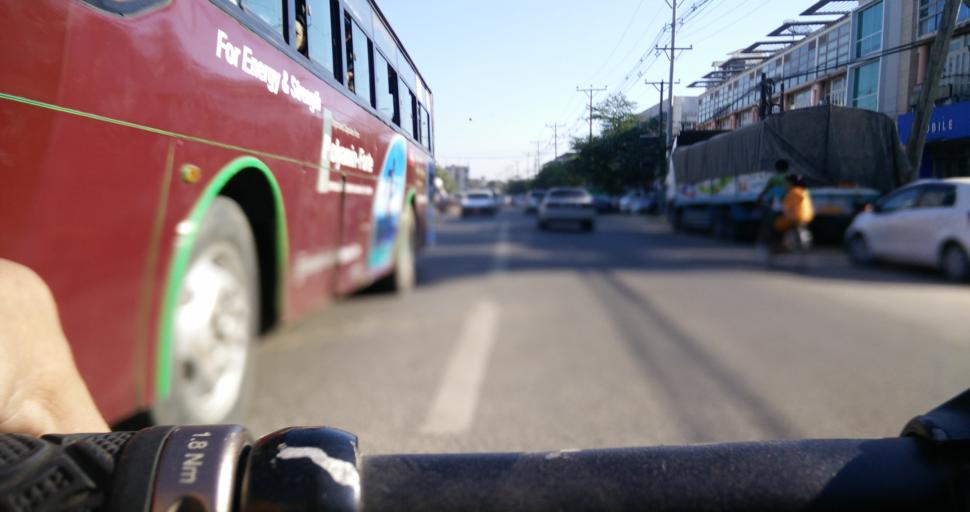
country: MM
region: Yangon
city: Yangon
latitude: 16.8434
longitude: 96.1982
